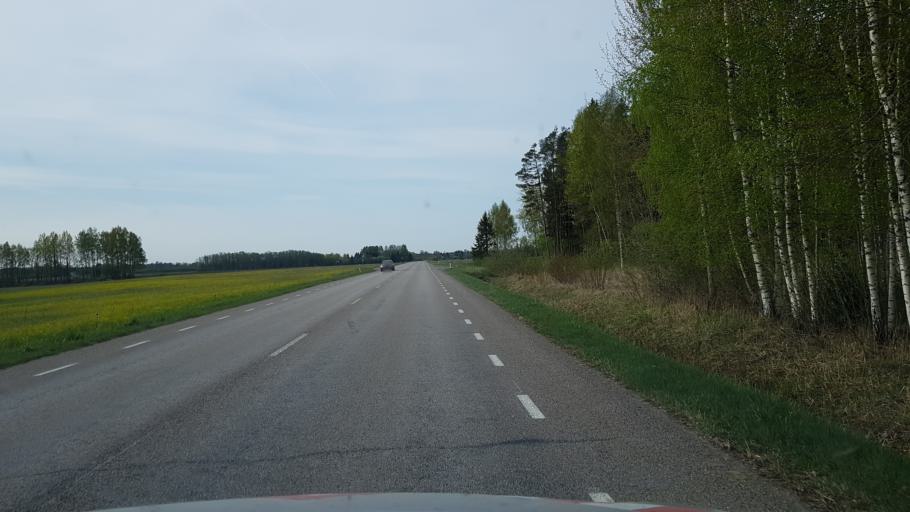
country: EE
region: Paernumaa
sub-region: Audru vald
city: Audru
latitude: 58.3817
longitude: 24.2719
